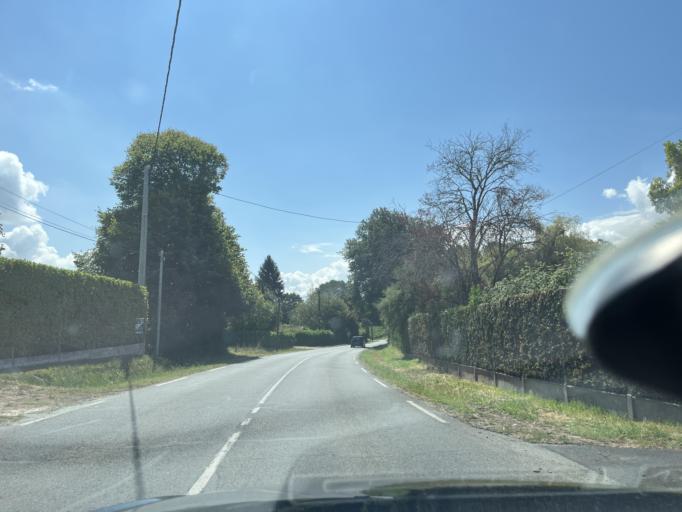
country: FR
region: Aquitaine
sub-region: Departement de la Gironde
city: Cars
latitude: 45.0966
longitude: -0.6395
